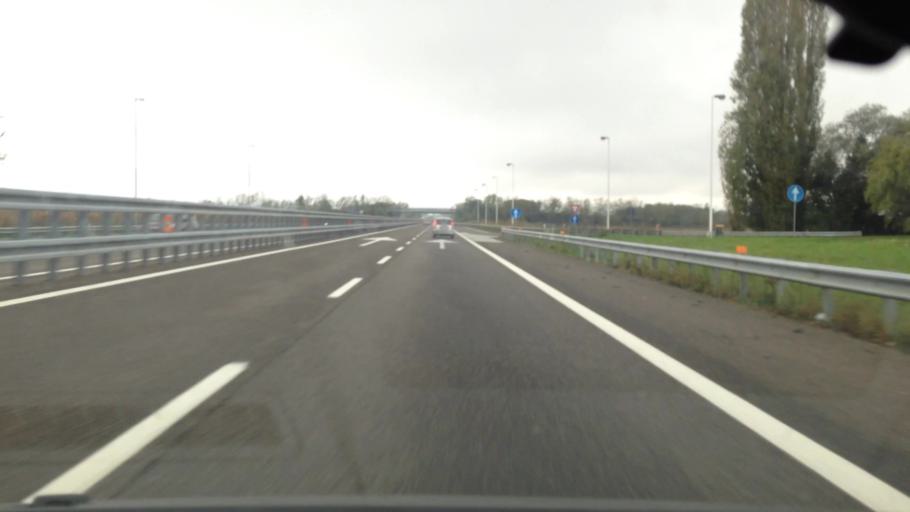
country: IT
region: Piedmont
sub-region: Provincia di Asti
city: Villanova d'Asti
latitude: 44.9502
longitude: 7.9494
